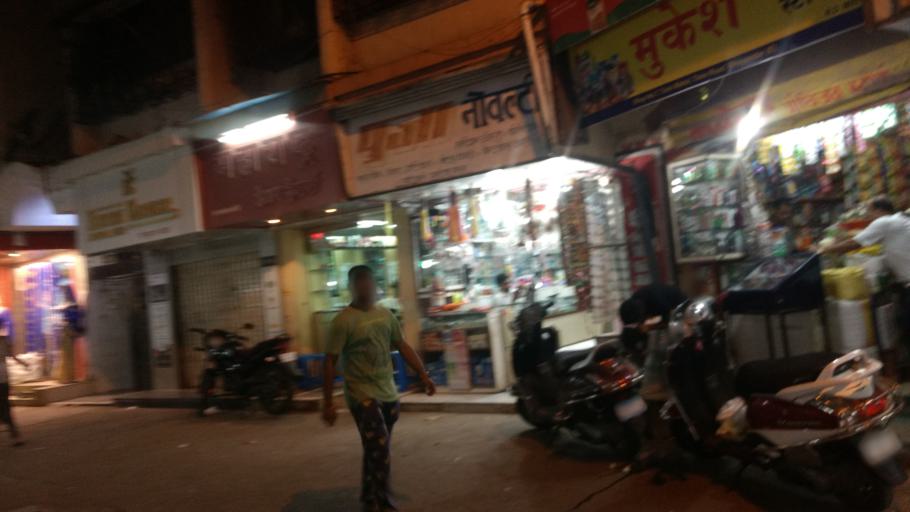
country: IN
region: Maharashtra
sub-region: Thane
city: Bhayandar
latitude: 19.3093
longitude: 72.8582
